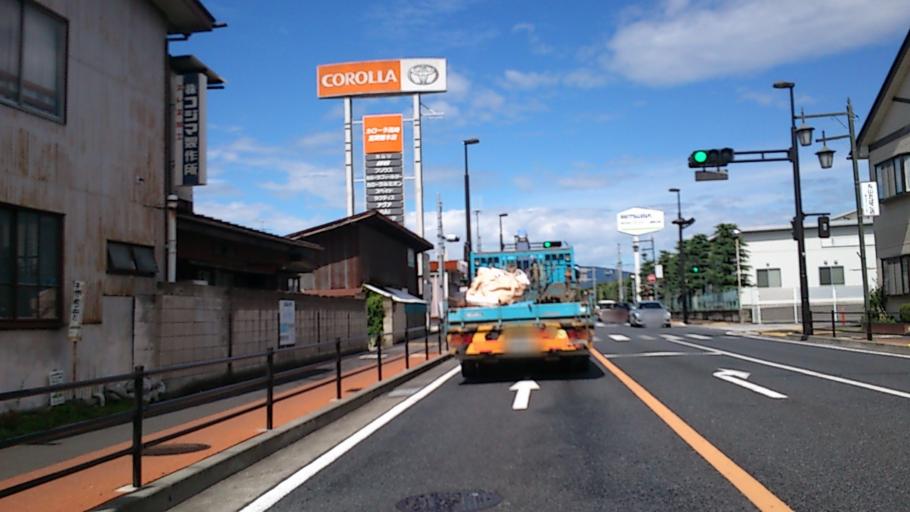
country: JP
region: Gunma
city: Tomioka
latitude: 36.2584
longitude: 138.9054
